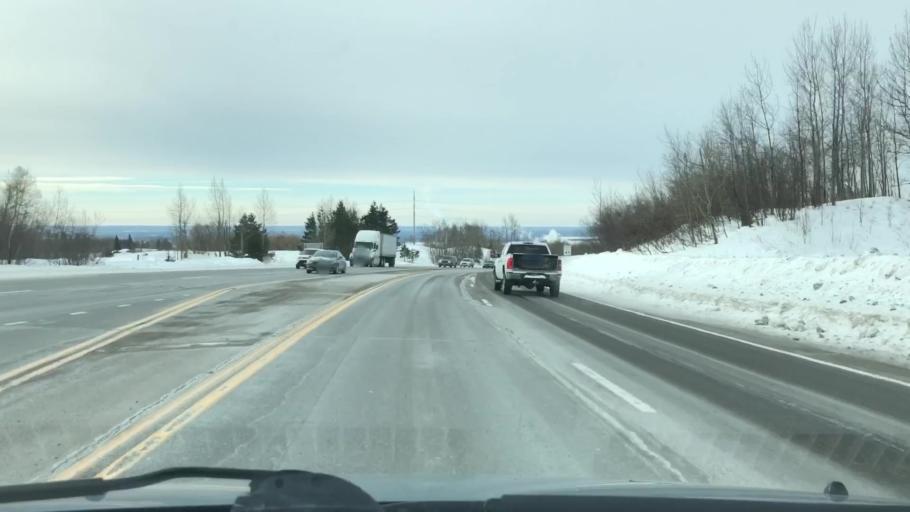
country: US
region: Minnesota
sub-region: Saint Louis County
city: Duluth
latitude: 46.7814
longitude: -92.1388
